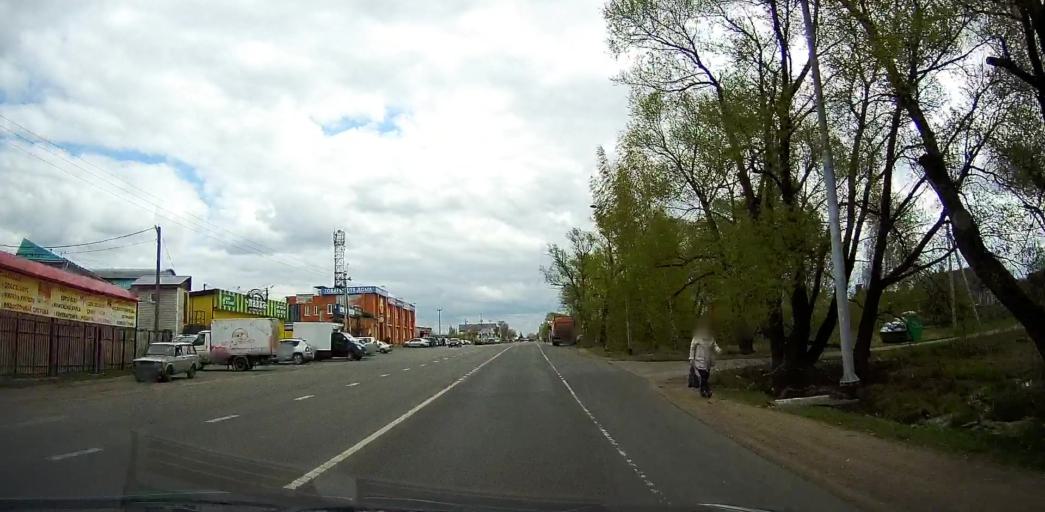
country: RU
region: Moskovskaya
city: Ashitkovo
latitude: 55.4282
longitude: 38.5484
